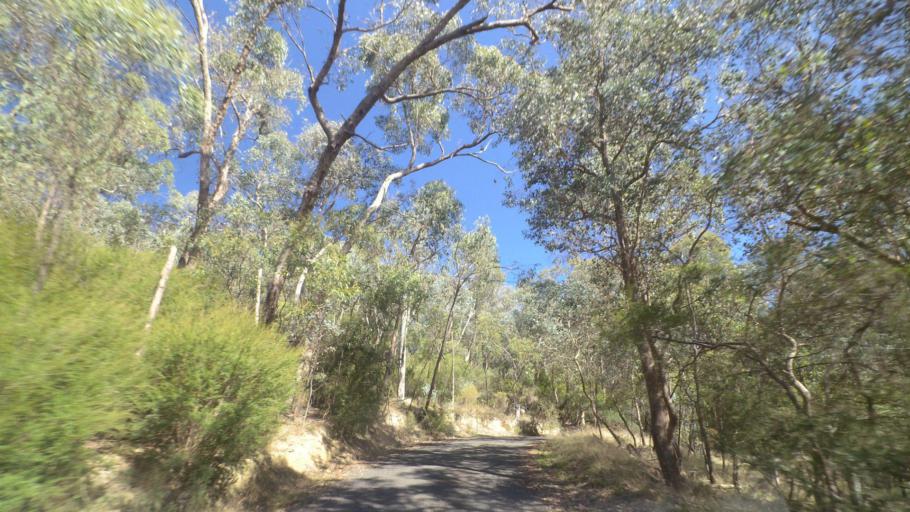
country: AU
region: Victoria
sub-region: Manningham
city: Warrandyte
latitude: -37.7483
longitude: 145.2262
